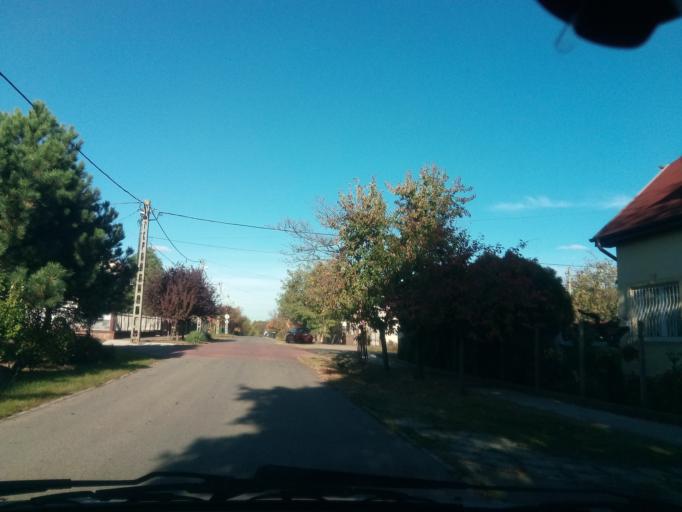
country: HU
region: Budapest
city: Budapest XVIII. keruelet
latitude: 47.4358
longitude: 19.2156
